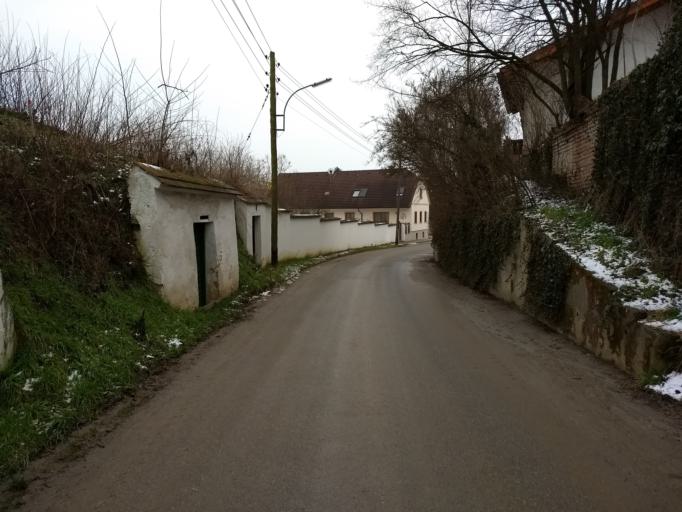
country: AT
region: Lower Austria
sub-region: Politischer Bezirk Mistelbach
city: Poysdorf
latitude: 48.6695
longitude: 16.6109
